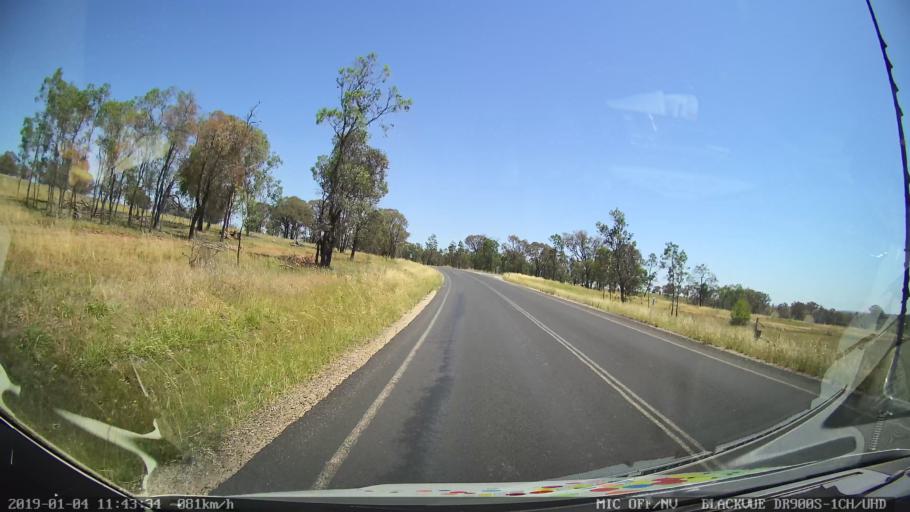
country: AU
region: New South Wales
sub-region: Cabonne
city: Molong
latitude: -32.9680
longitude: 148.7838
